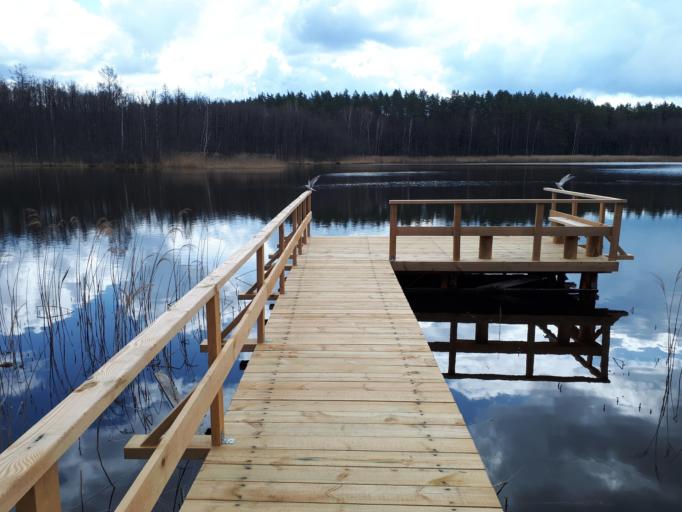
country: LT
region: Alytaus apskritis
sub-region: Alytaus rajonas
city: Daugai
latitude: 54.1689
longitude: 24.2139
